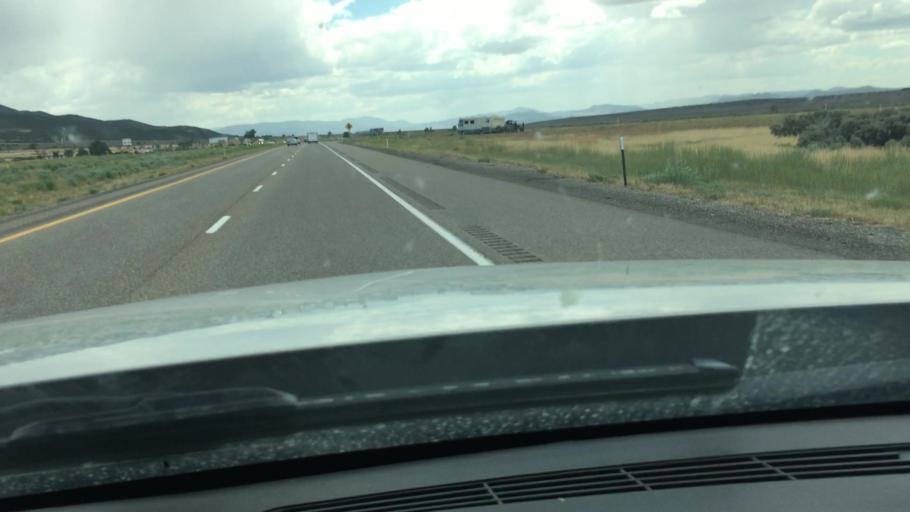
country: US
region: Utah
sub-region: Iron County
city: Enoch
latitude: 37.8018
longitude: -112.9480
